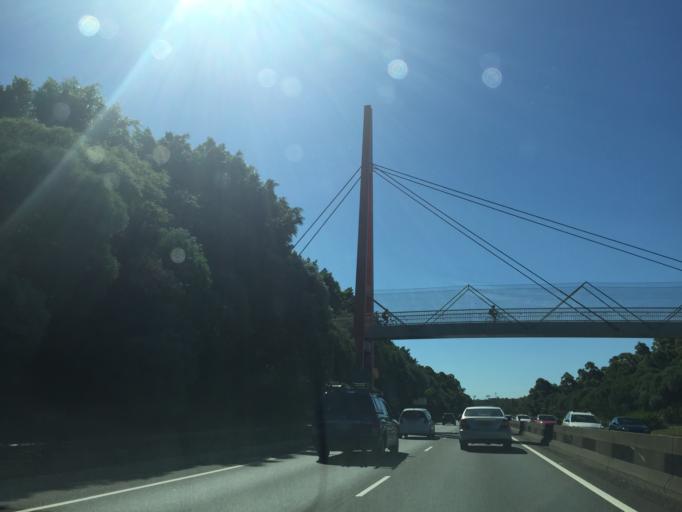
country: AU
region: New South Wales
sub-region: Strathfield
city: Homebush
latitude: -33.8613
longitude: 151.0803
